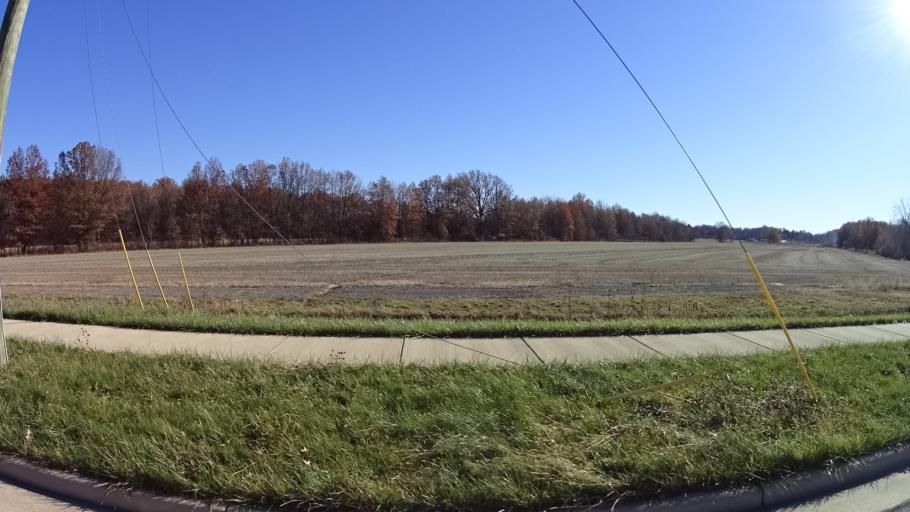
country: US
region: Ohio
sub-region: Lorain County
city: Avon Center
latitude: 41.4630
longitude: -81.9870
